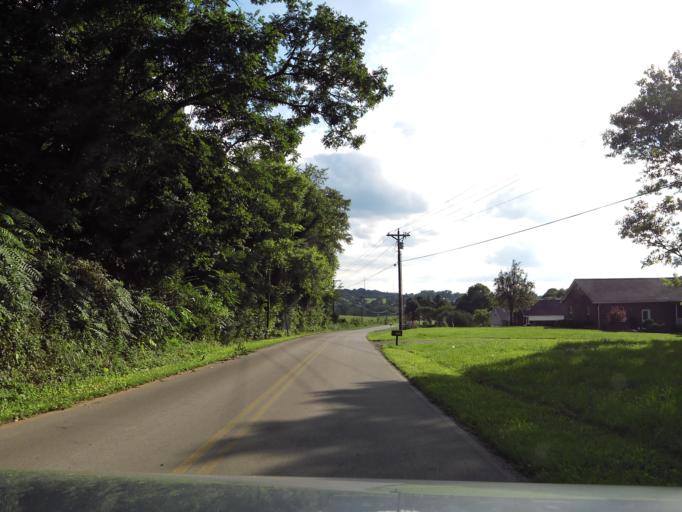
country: US
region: Tennessee
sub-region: Loudon County
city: Greenback
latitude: 35.6607
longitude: -84.0950
